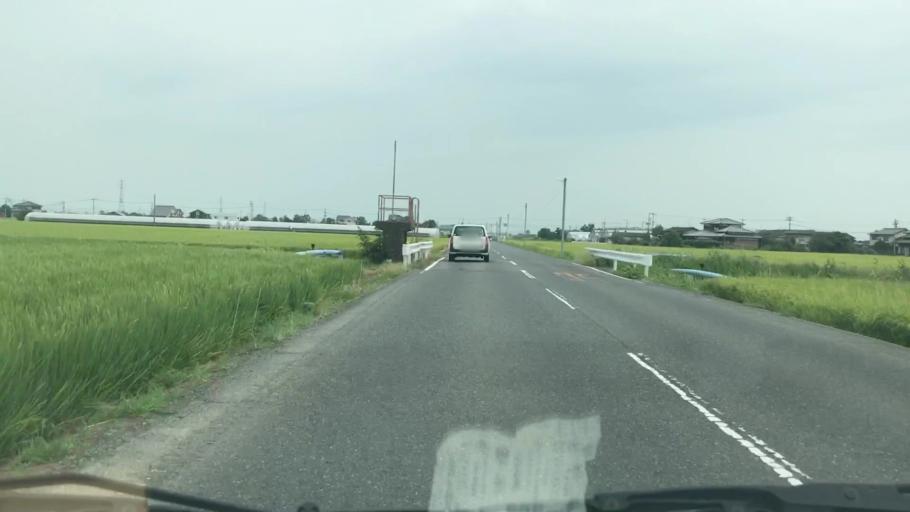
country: JP
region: Saga Prefecture
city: Saga-shi
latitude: 33.2280
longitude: 130.2974
